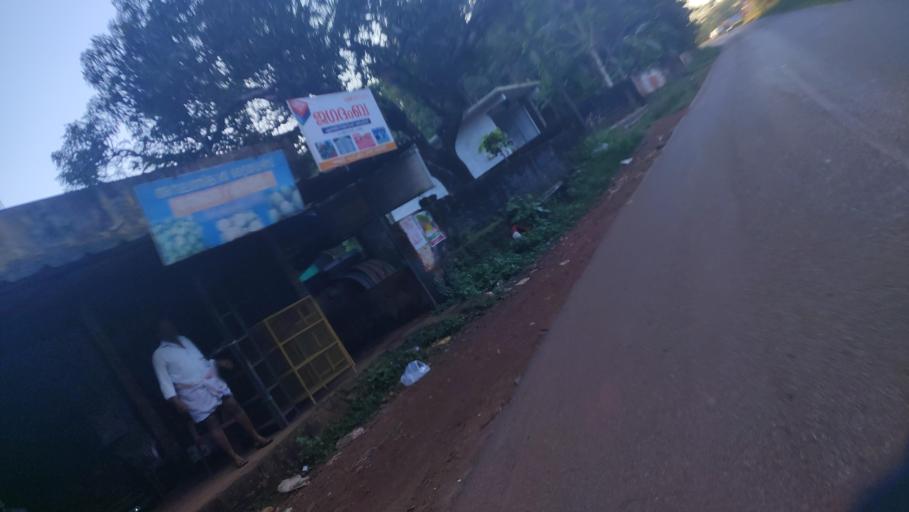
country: IN
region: Kerala
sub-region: Kasaragod District
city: Kannangad
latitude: 12.3994
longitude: 75.0634
